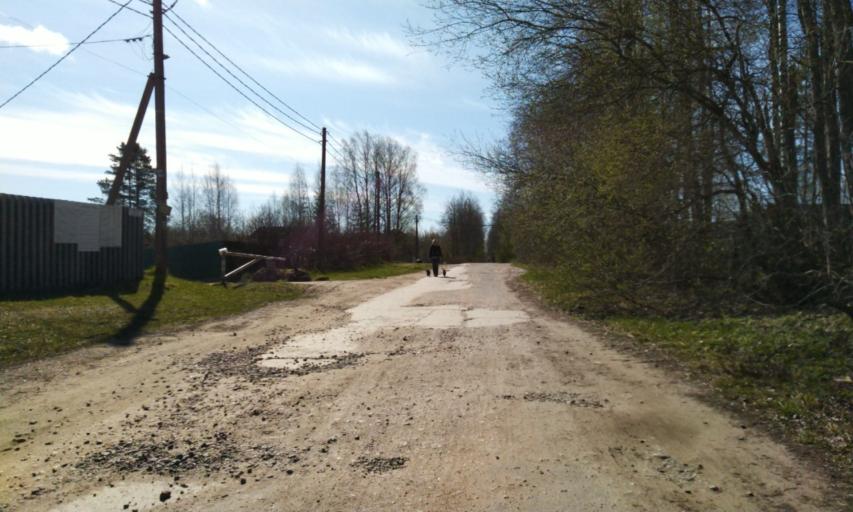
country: RU
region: Leningrad
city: Garbolovo
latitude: 60.3901
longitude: 30.4806
